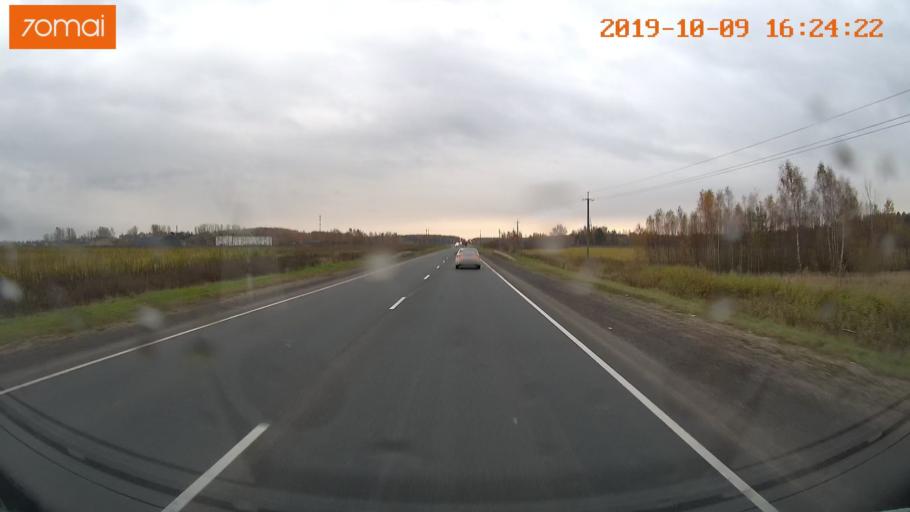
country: RU
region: Kostroma
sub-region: Kostromskoy Rayon
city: Kostroma
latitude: 57.6530
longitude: 40.9097
